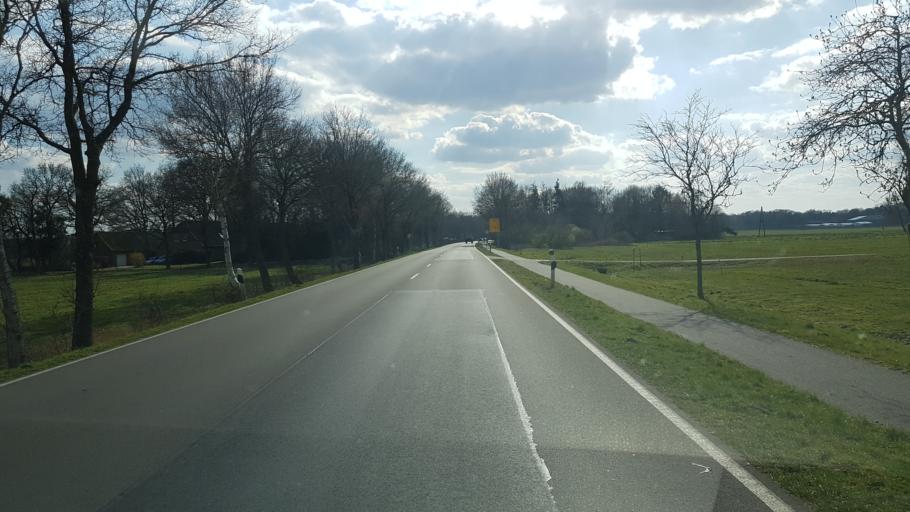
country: DE
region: Lower Saxony
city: Rastede
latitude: 53.2384
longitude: 8.2833
